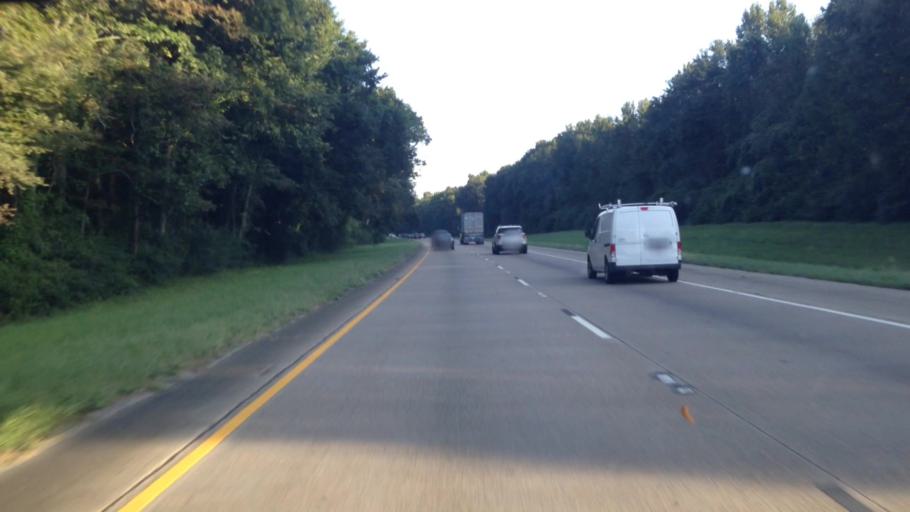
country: US
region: Louisiana
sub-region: Ascension Parish
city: Prairieville
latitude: 30.3069
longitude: -90.9939
